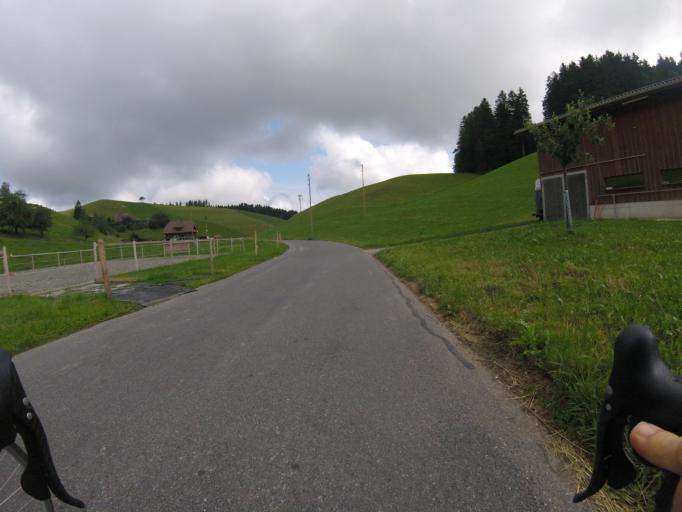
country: CH
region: Bern
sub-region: Bern-Mittelland District
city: Vechigen
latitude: 46.9751
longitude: 7.5798
